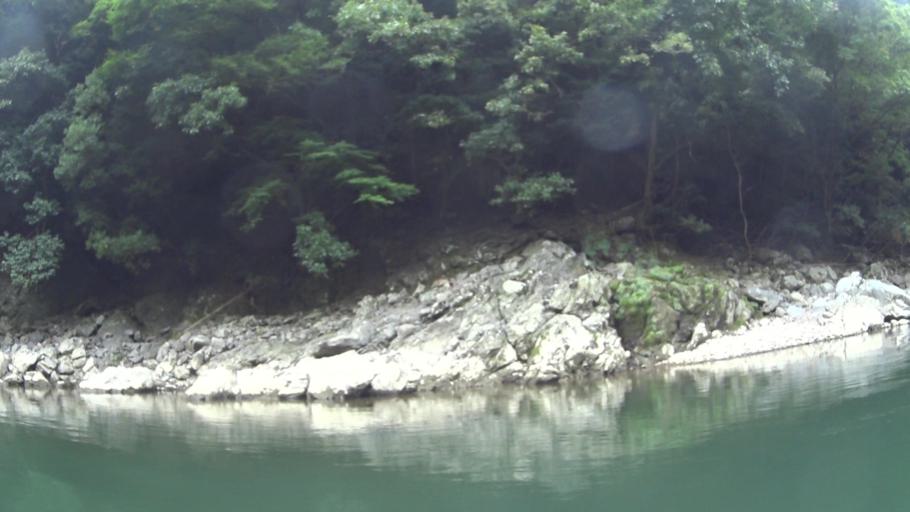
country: JP
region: Kyoto
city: Kameoka
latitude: 35.0204
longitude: 135.6224
